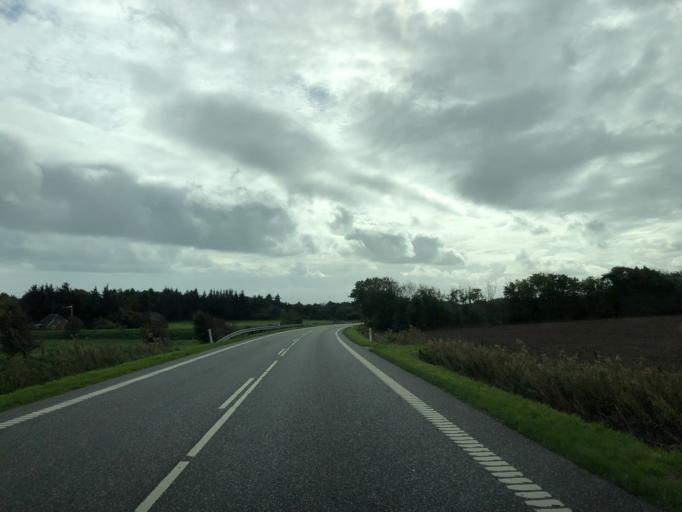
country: DK
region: North Denmark
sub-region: Thisted Kommune
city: Hurup
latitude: 56.6916
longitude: 8.4017
